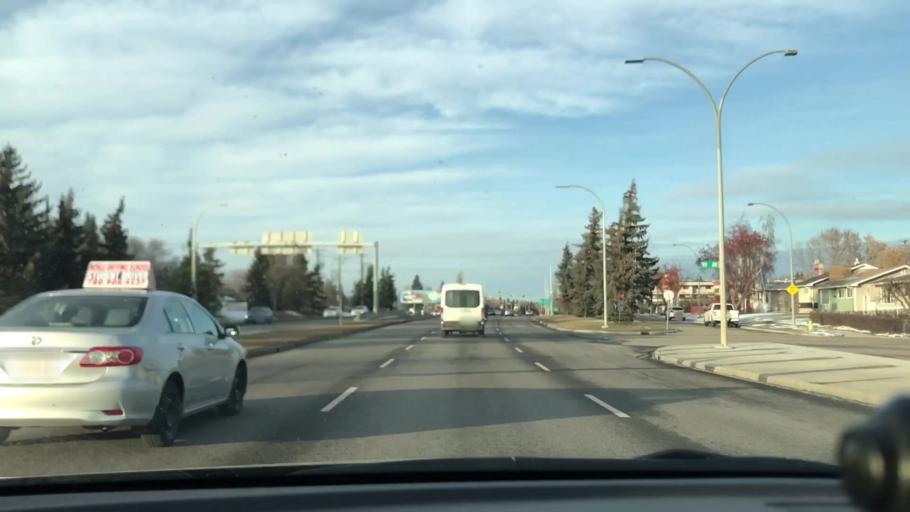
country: CA
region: Alberta
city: Edmonton
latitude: 53.5390
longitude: -113.4432
